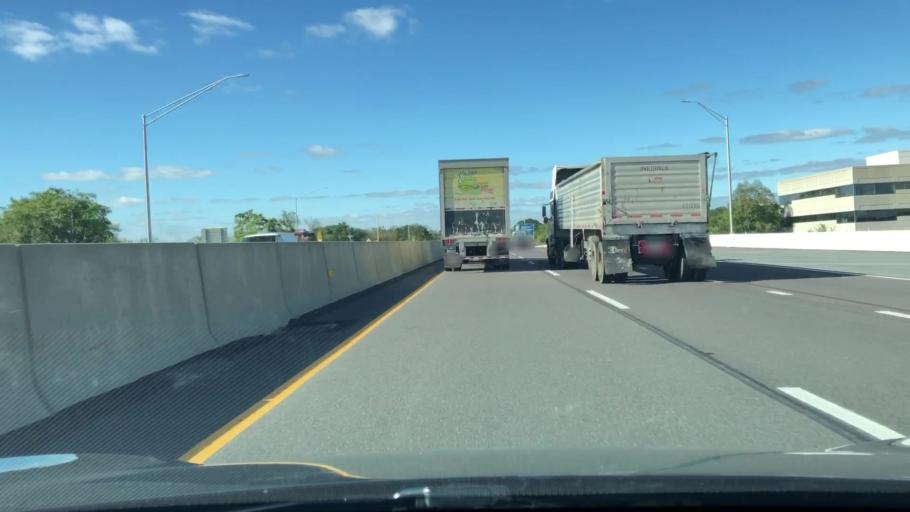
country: US
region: Pennsylvania
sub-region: Montgomery County
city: King of Prussia
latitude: 40.0913
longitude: -75.4109
